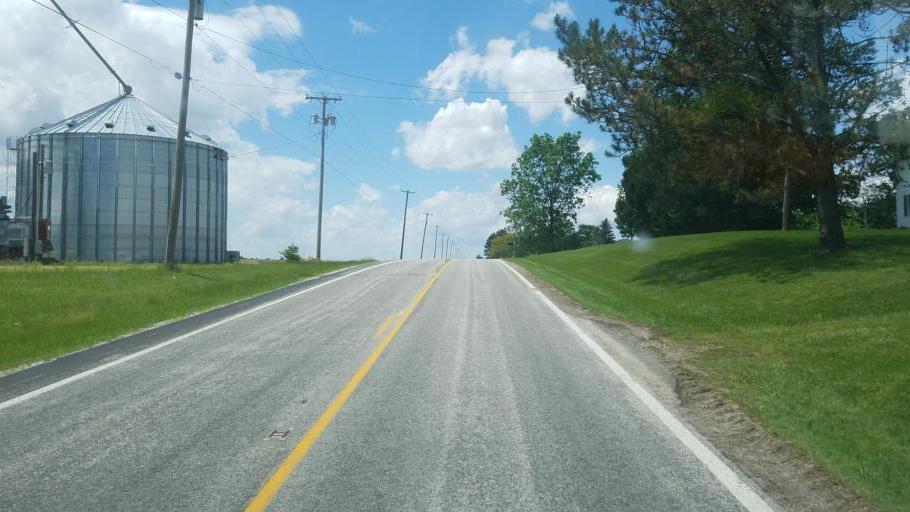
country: US
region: Ohio
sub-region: Huron County
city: Willard
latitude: 41.1051
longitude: -82.6914
